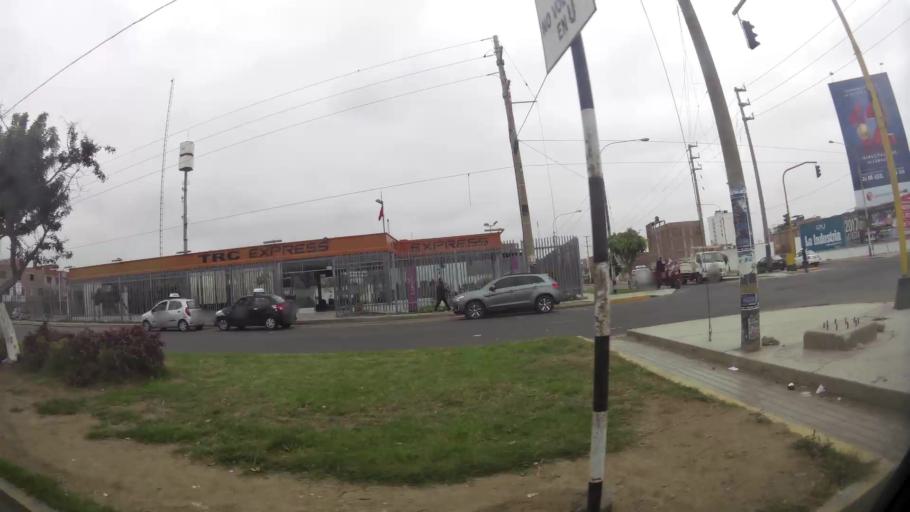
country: PE
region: La Libertad
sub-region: Provincia de Trujillo
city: Trujillo
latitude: -8.1066
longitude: -79.0468
